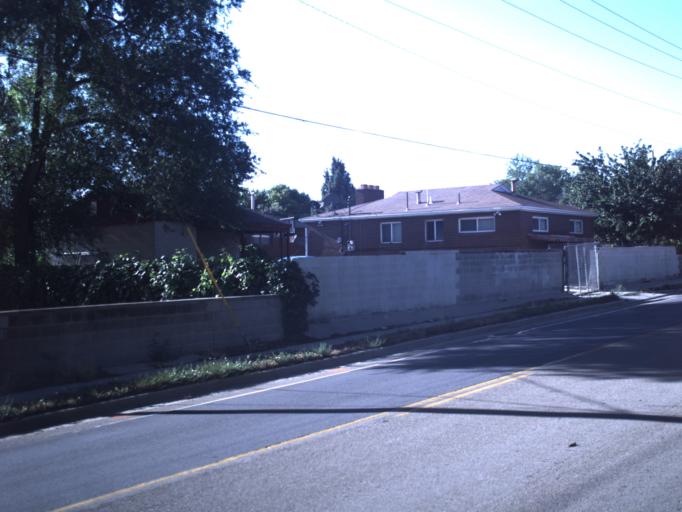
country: US
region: Utah
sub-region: Salt Lake County
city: Magna
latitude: 40.7003
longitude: -112.0919
